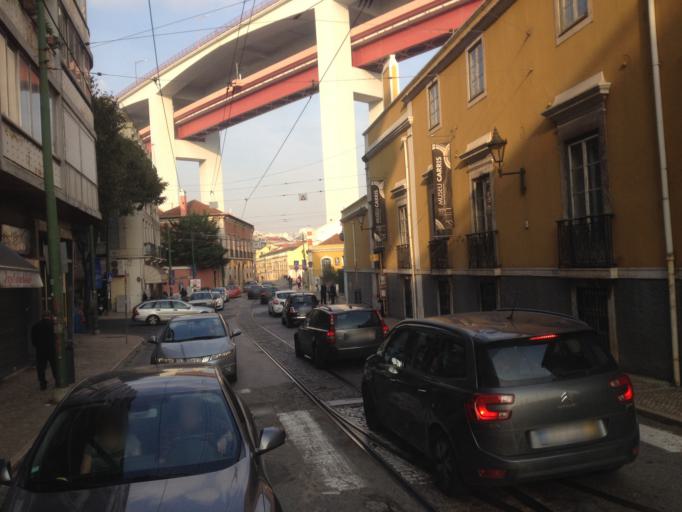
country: PT
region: Setubal
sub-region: Almada
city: Pragal
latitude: 38.7021
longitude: -9.1804
